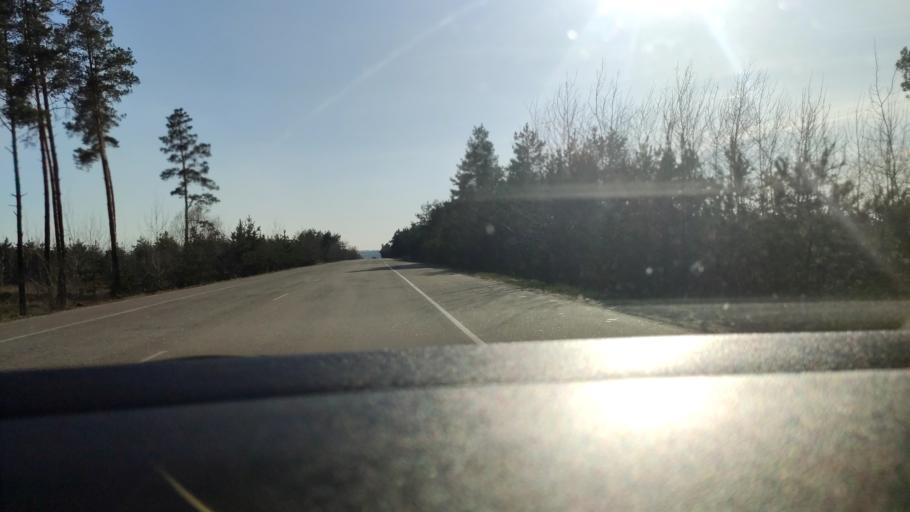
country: RU
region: Voronezj
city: Kolodeznyy
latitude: 51.3660
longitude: 39.1961
